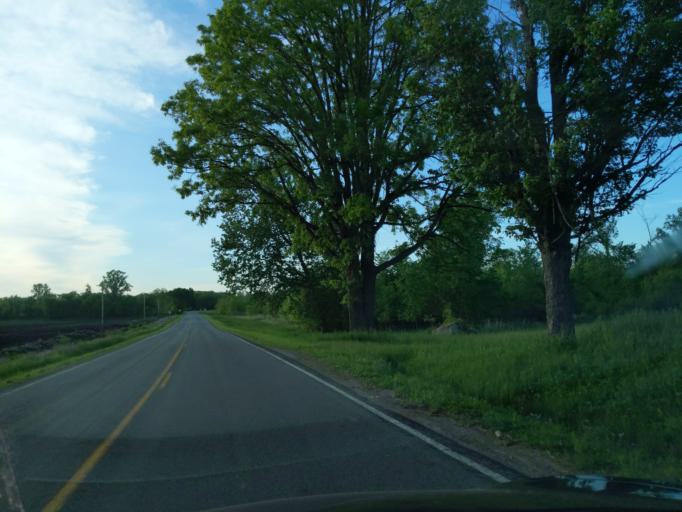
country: US
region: Michigan
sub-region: Ingham County
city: Leslie
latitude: 42.4635
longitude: -84.3149
